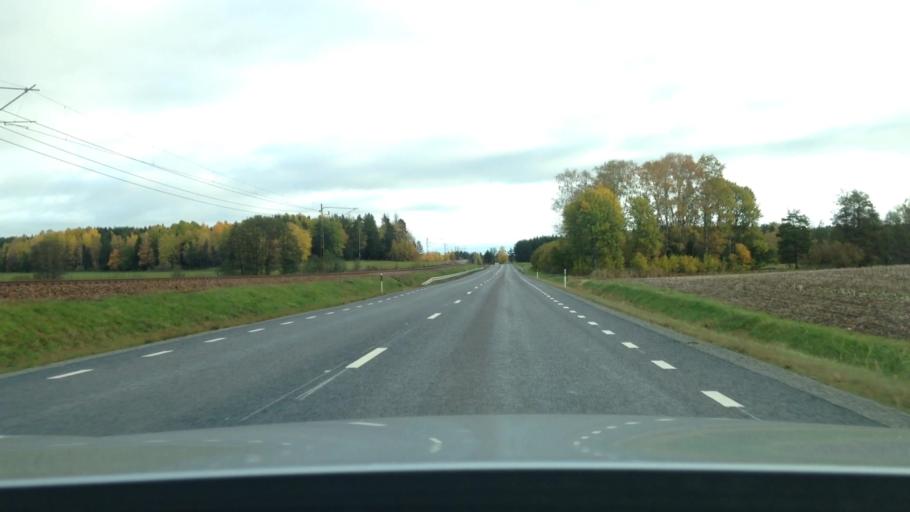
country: SE
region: Vaermland
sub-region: Saffle Kommun
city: Saeffle
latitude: 59.1623
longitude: 12.9946
